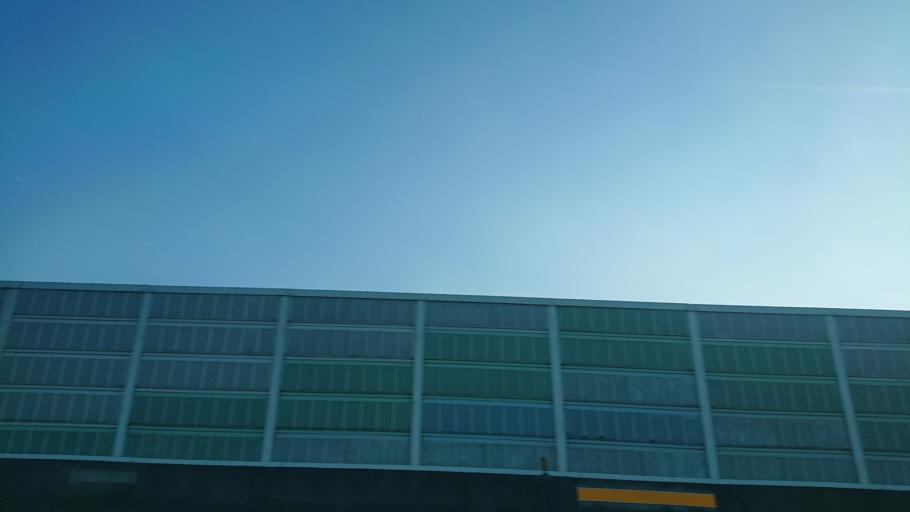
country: TW
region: Taiwan
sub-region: Changhua
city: Chang-hua
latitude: 24.1118
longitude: 120.6055
